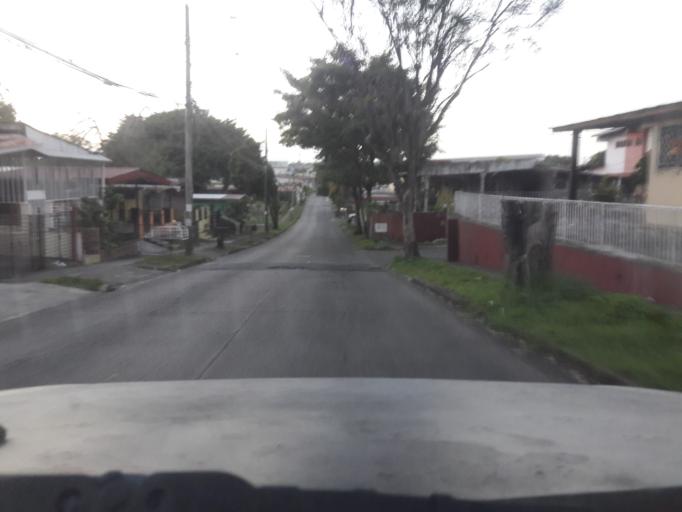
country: PA
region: Panama
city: San Miguelito
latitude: 9.0534
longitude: -79.4364
